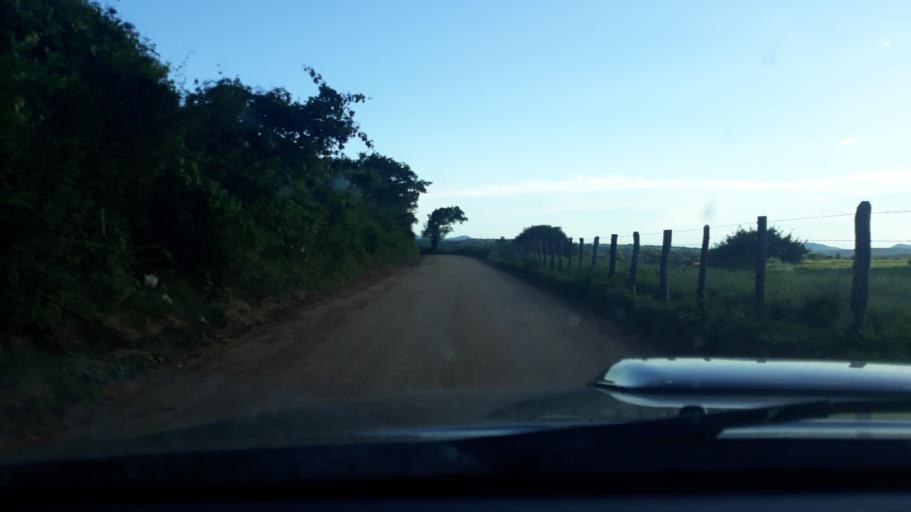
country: BR
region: Bahia
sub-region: Riacho De Santana
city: Riacho de Santana
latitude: -13.8184
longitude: -42.7239
